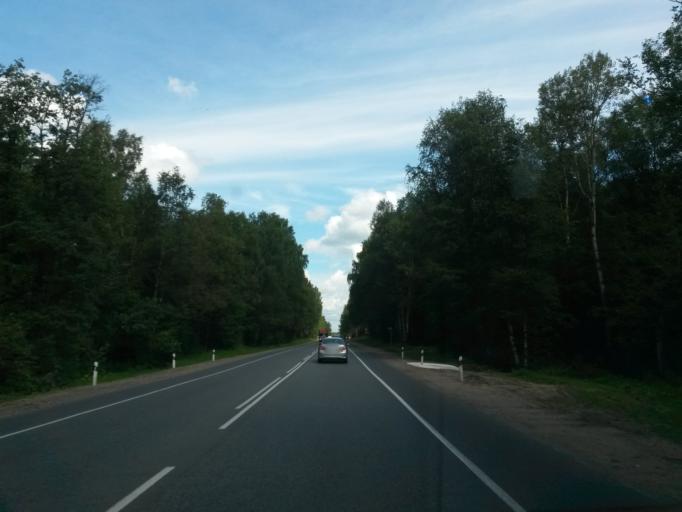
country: RU
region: Jaroslavl
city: Pereslavl'-Zalesskiy
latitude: 56.8148
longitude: 38.9019
